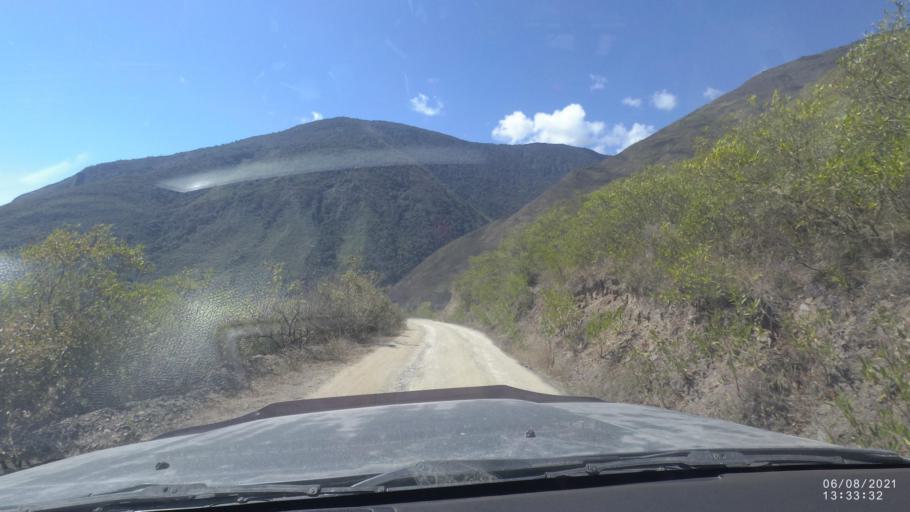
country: BO
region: La Paz
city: Quime
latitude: -16.6974
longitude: -66.7263
